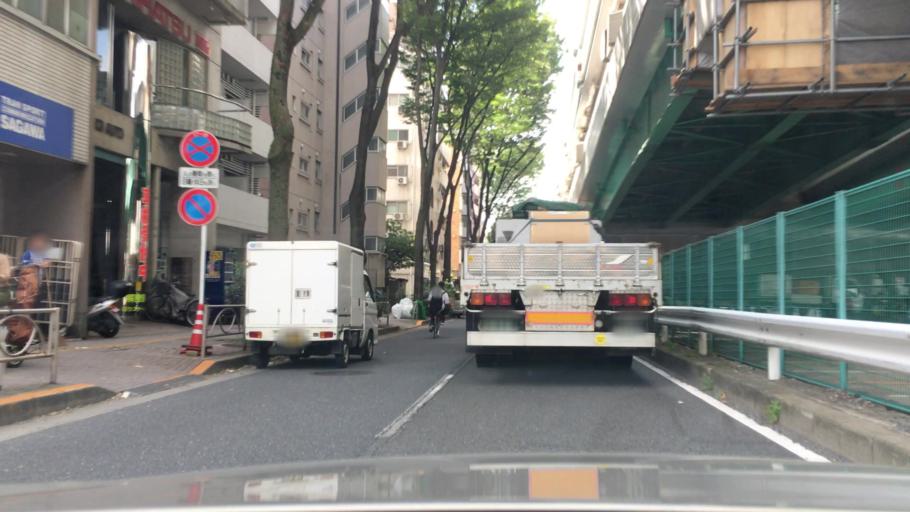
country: JP
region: Tokyo
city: Tokyo
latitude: 35.6705
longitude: 139.6528
